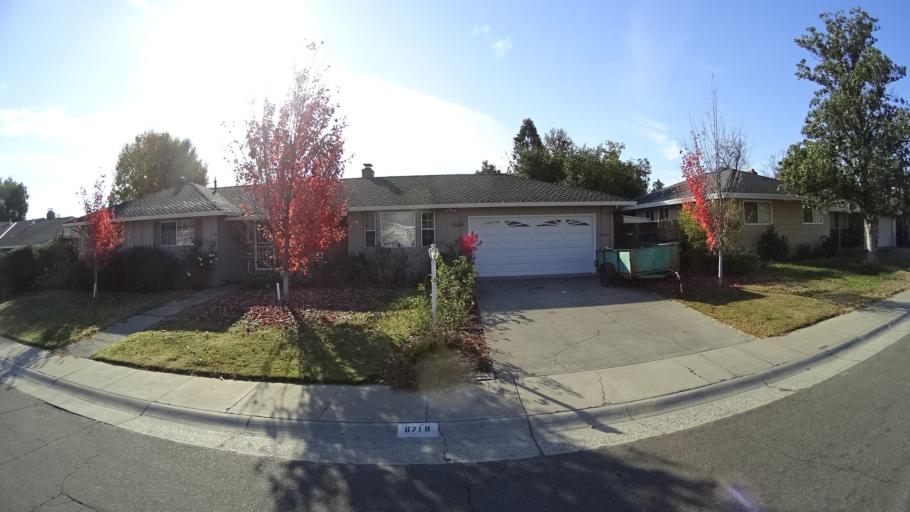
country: US
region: California
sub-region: Sacramento County
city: Antelope
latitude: 38.6790
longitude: -121.3069
